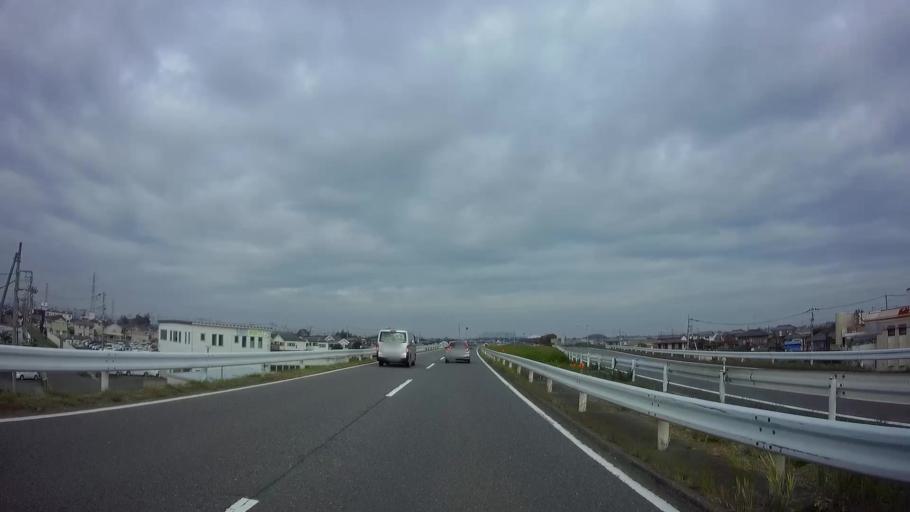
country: JP
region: Saitama
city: Gyoda
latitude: 36.1392
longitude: 139.4313
